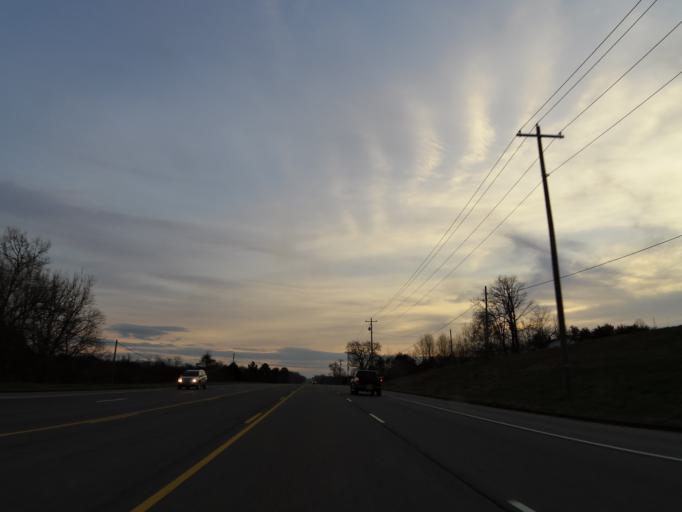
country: US
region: Tennessee
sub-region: McMinn County
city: Englewood
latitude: 35.4173
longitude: -84.4923
